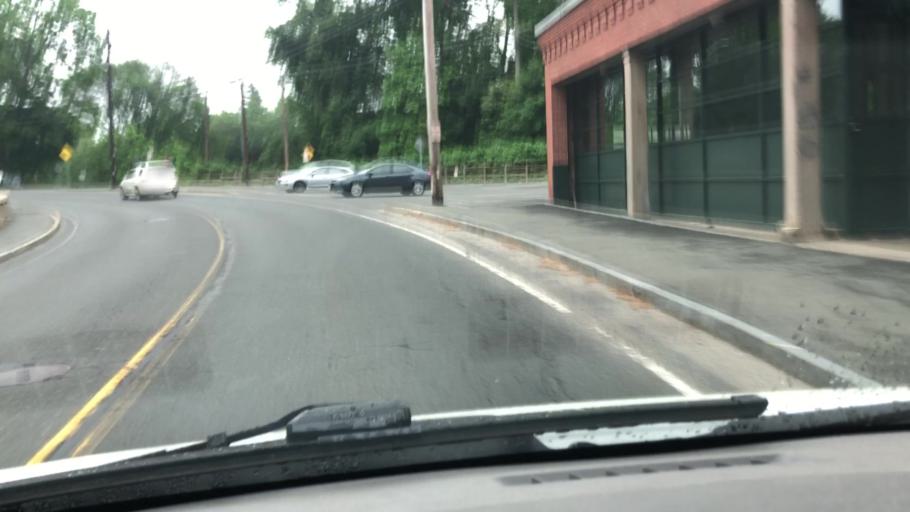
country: US
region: Massachusetts
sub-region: Hampshire County
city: Northampton
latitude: 42.3135
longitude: -72.6384
